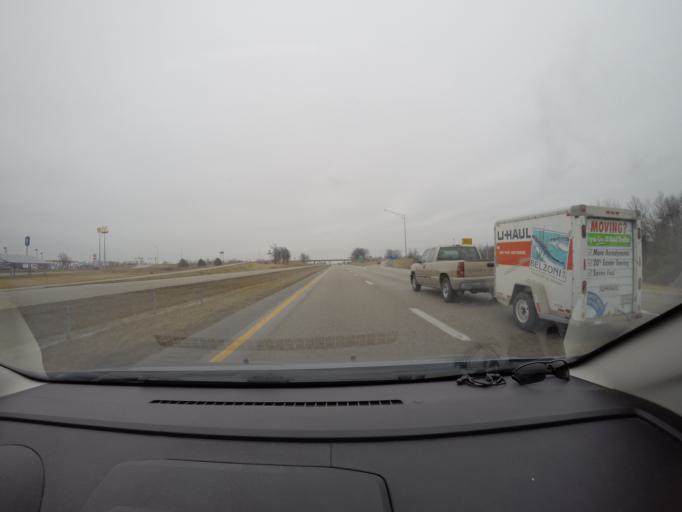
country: US
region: Missouri
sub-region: Montgomery County
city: Montgomery City
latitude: 38.9006
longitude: -91.4604
